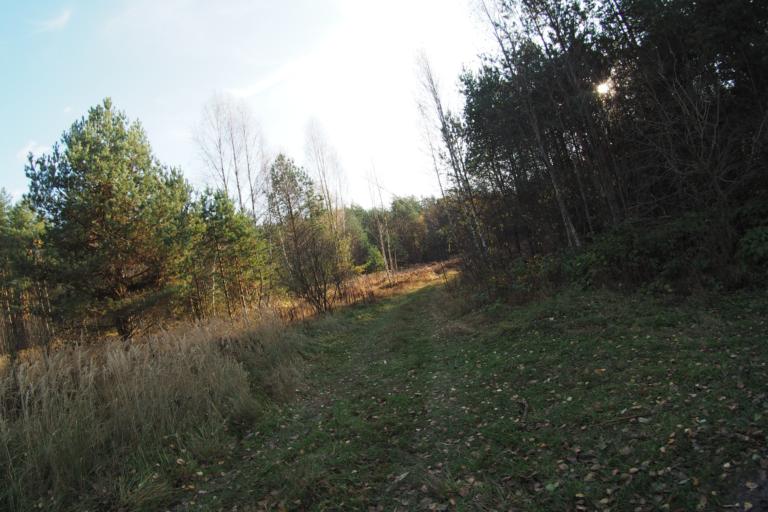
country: RU
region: Moskovskaya
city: Davydovo
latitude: 55.5452
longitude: 38.8204
